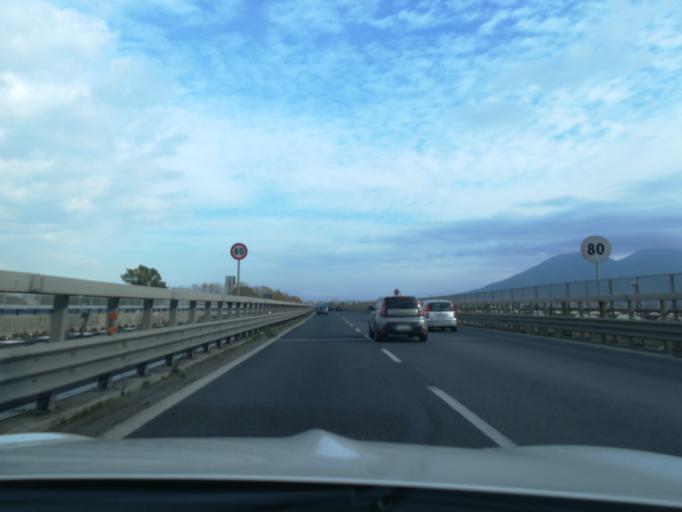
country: IT
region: Campania
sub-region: Provincia di Napoli
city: Arpino
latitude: 40.8645
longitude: 14.3003
